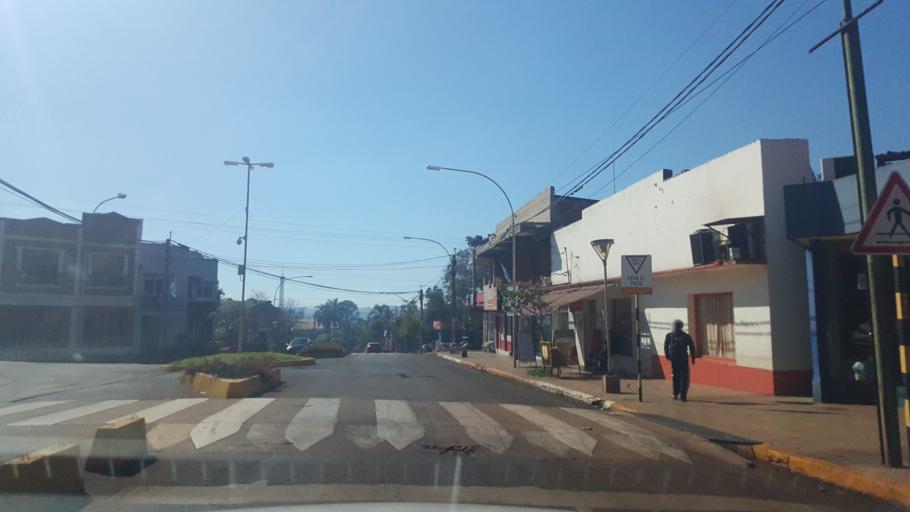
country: AR
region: Misiones
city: Puerto Rico
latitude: -26.8078
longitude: -55.0253
